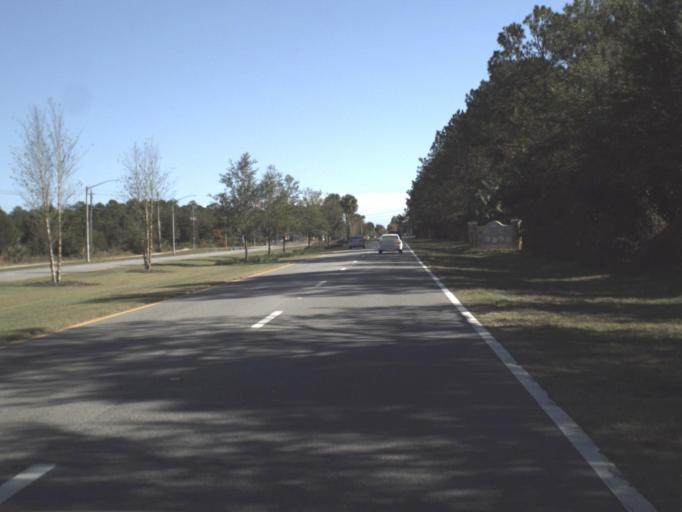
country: US
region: Florida
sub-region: Flagler County
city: Palm Coast
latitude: 29.5528
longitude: -81.2617
